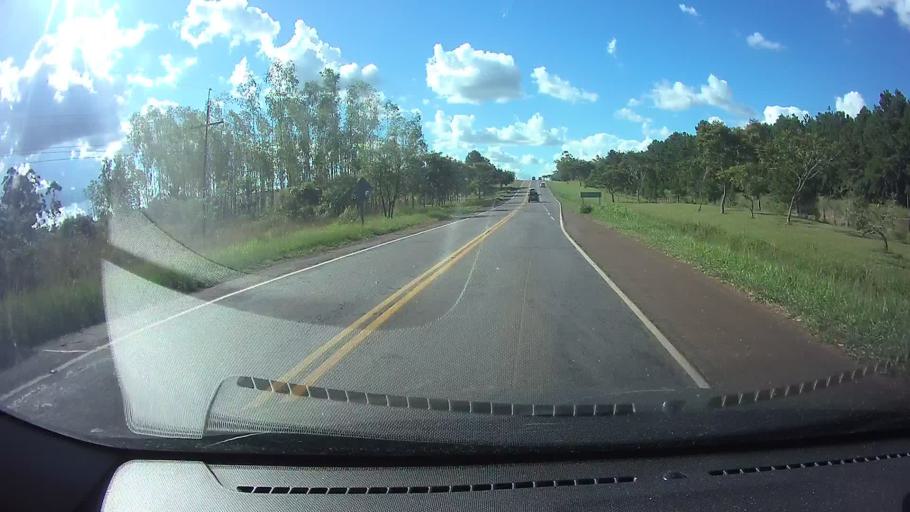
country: PY
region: Cordillera
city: Itacurubi de la Cordillera
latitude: -25.4517
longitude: -56.9002
